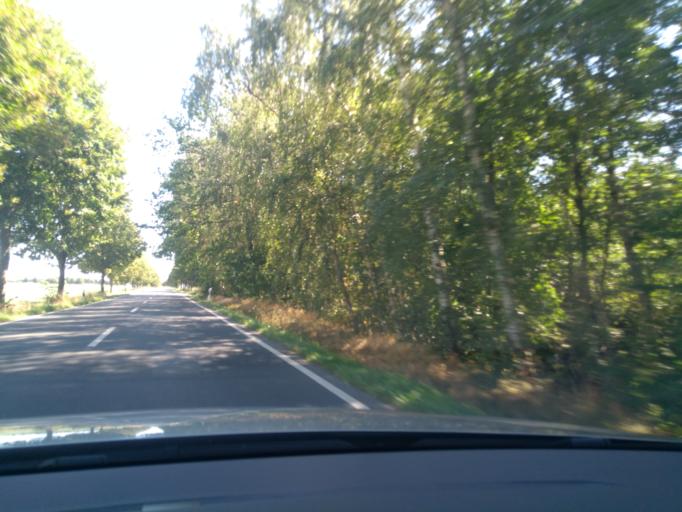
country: DE
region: Saxony
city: Crostwitz
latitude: 51.2168
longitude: 14.2644
